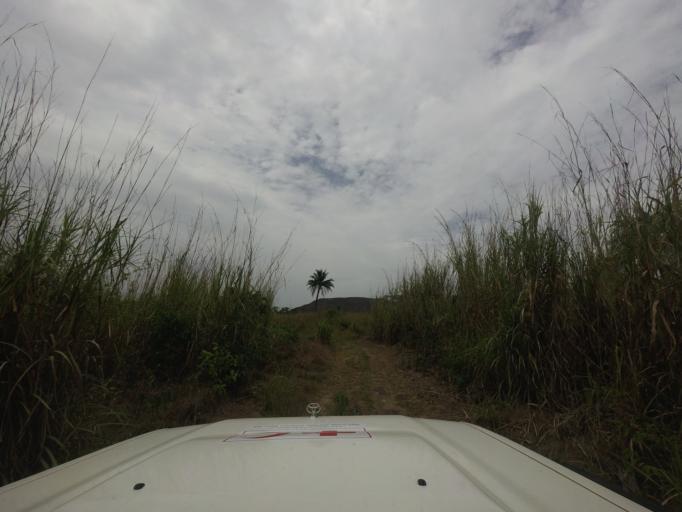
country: SL
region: Eastern Province
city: Buedu
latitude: 8.4259
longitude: -10.2628
